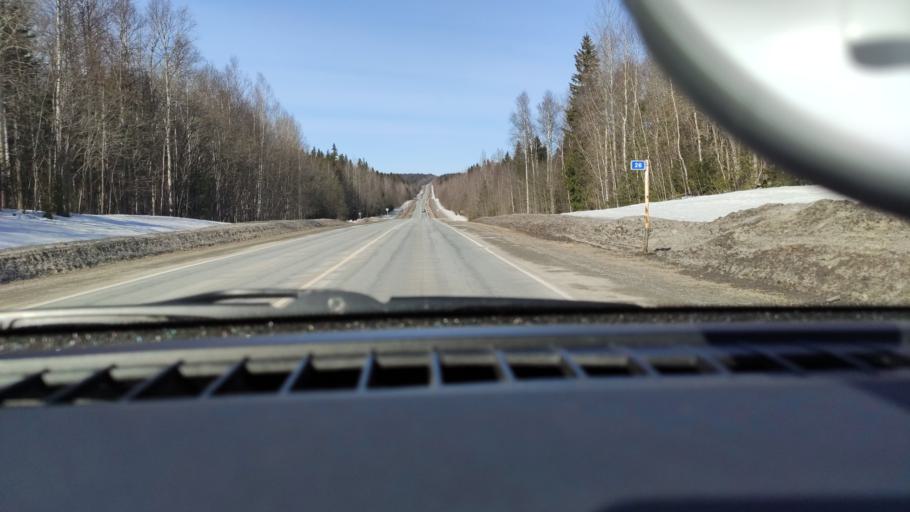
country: RU
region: Perm
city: Perm
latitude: 58.1535
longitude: 56.2540
